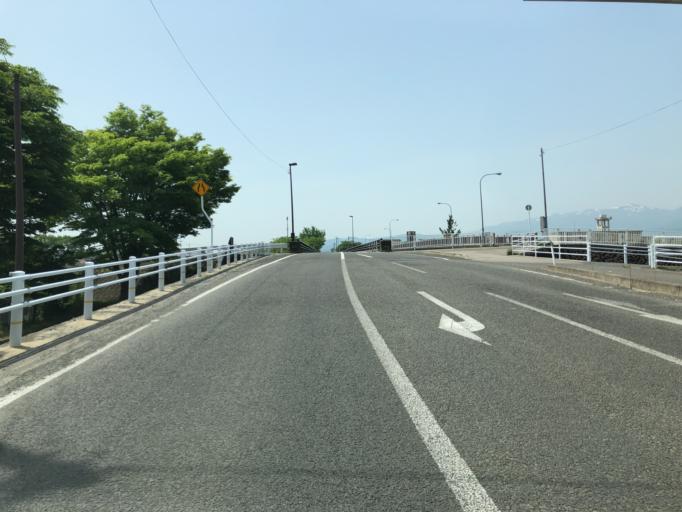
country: JP
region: Fukushima
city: Fukushima-shi
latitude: 37.7829
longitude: 140.4265
